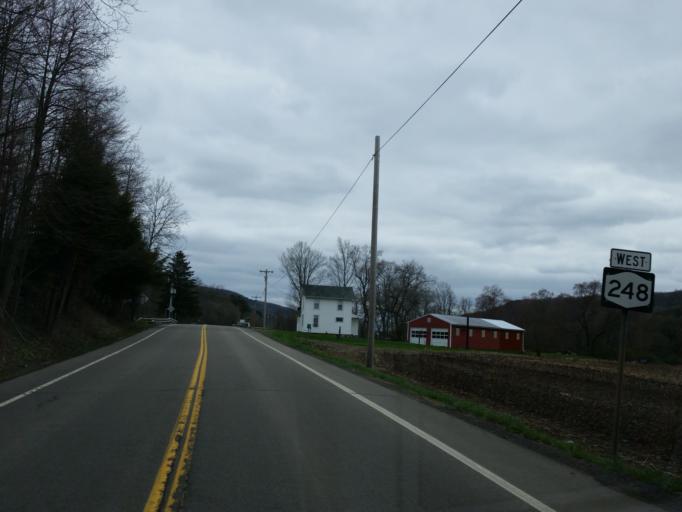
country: US
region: New York
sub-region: Allegany County
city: Andover
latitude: 42.0483
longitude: -77.7500
